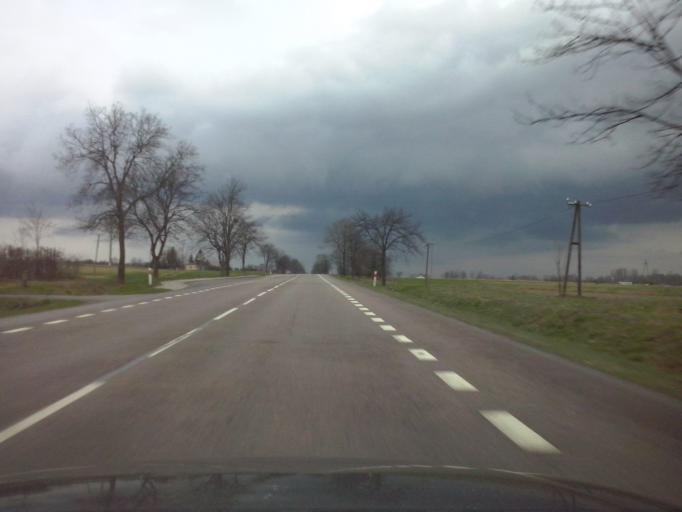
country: PL
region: Lublin Voivodeship
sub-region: Powiat chelmski
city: Rejowiec Fabryczny
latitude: 51.1756
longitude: 23.2481
